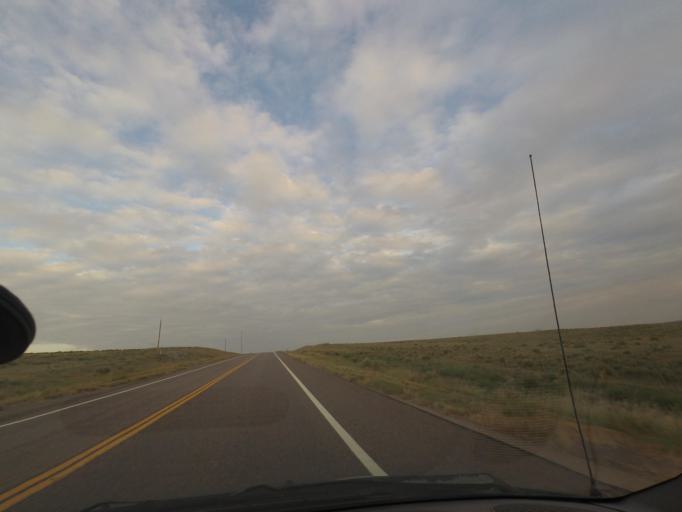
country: US
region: Kansas
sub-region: Cheyenne County
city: Saint Francis
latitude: 39.7467
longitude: -102.0801
